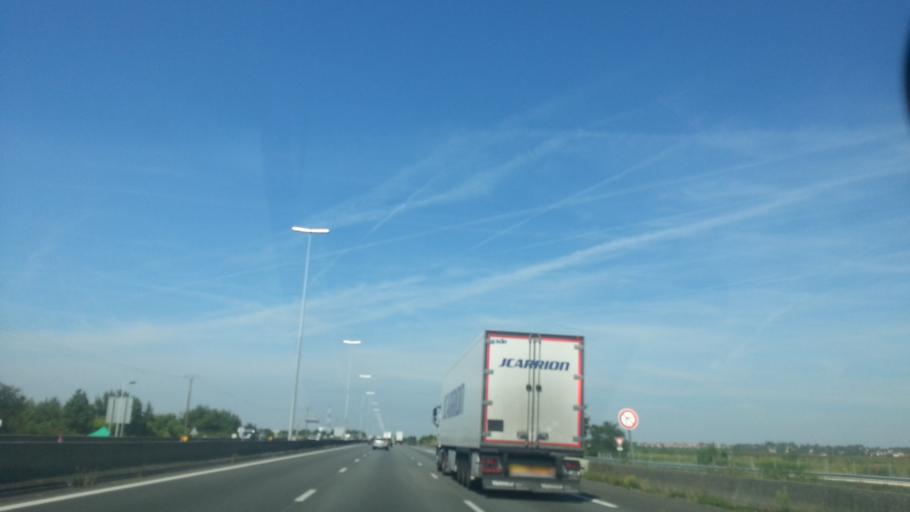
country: FR
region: Ile-de-France
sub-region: Departement du Val-d'Oise
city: Vemars
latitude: 49.0743
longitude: 2.5520
